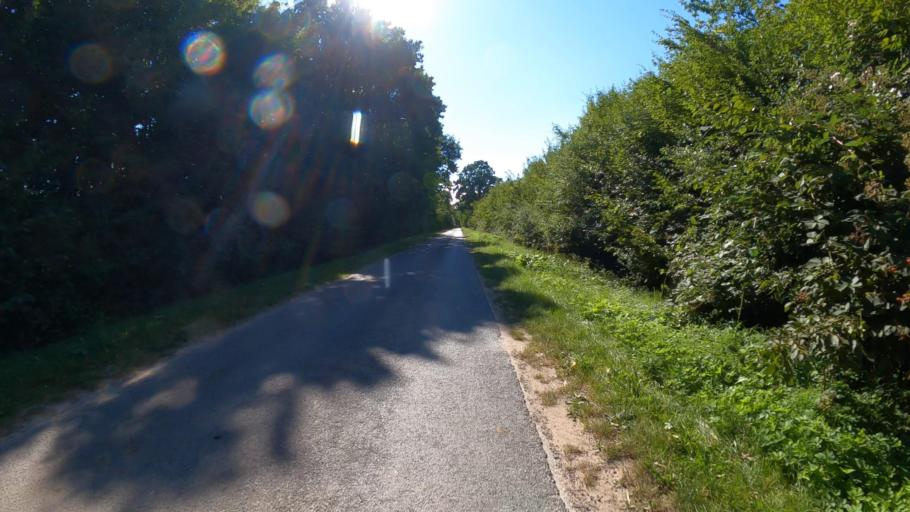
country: DE
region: Schleswig-Holstein
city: Schurensohlen
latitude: 53.7532
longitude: 10.4799
